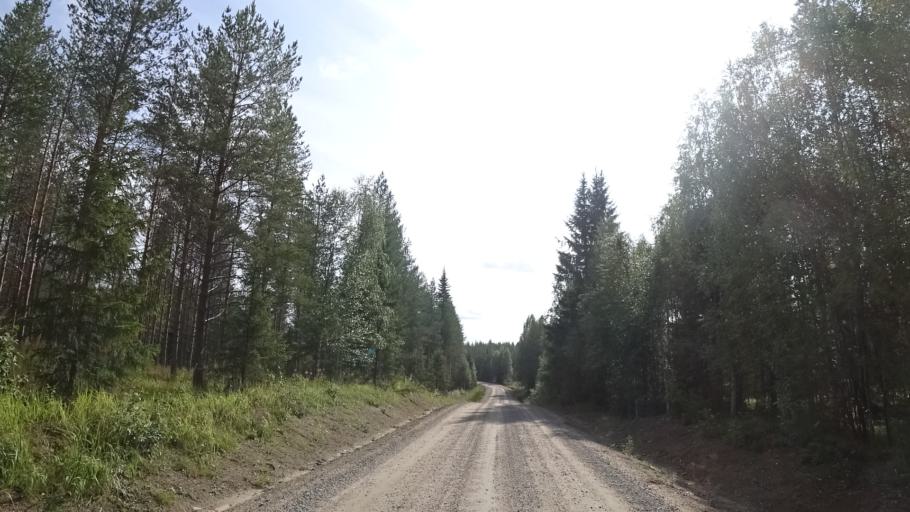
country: FI
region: North Karelia
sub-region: Pielisen Karjala
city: Lieksa
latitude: 63.5931
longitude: 30.1375
